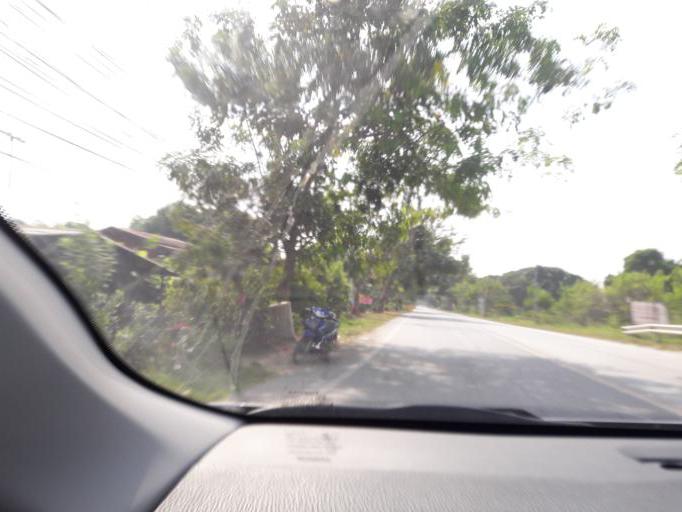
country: TH
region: Ang Thong
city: Ang Thong
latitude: 14.5596
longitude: 100.4421
